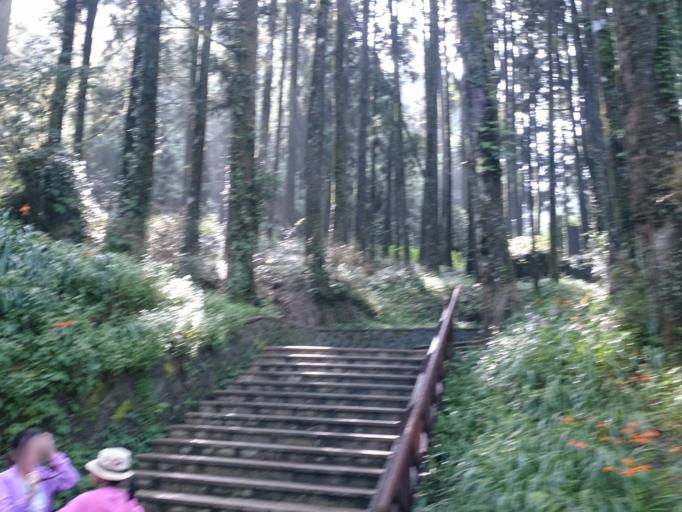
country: TW
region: Taiwan
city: Lugu
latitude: 23.5141
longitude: 120.8102
